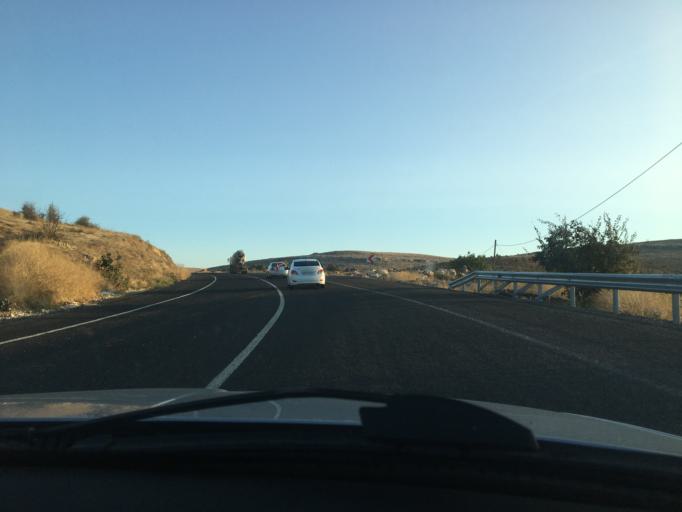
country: TR
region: Sanliurfa
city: Halfeti
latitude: 37.1936
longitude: 37.9669
